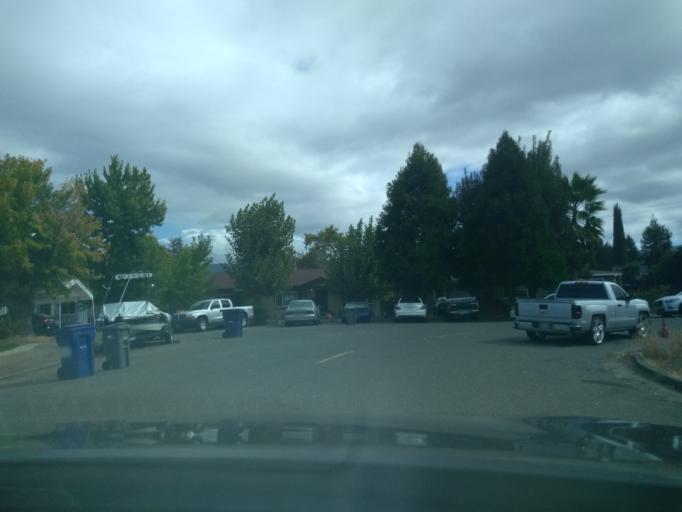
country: US
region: California
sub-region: Mendocino County
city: Ukiah
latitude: 39.1286
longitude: -123.2068
